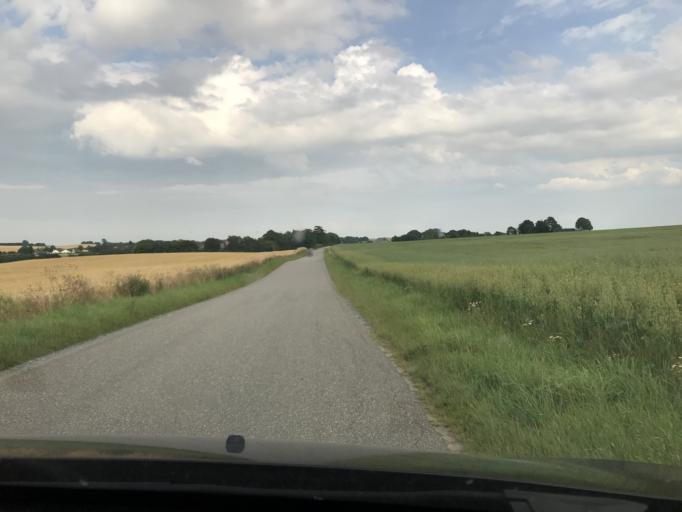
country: DK
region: South Denmark
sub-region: Vejle Kommune
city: Jelling
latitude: 55.8029
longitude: 9.4468
